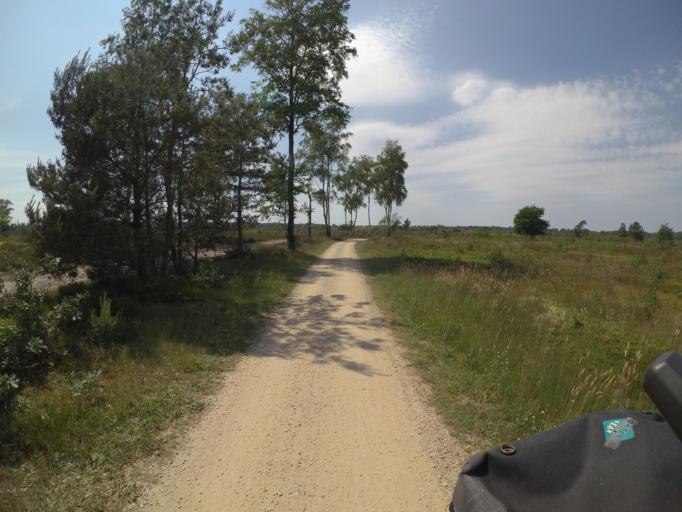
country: NL
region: Overijssel
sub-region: Gemeente Hof van Twente
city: Markelo
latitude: 52.3426
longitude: 6.4497
